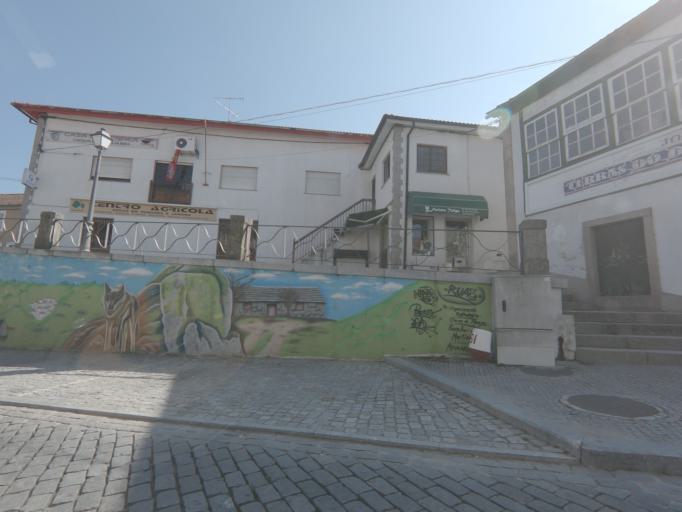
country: PT
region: Viseu
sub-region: Moimenta da Beira
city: Moimenta da Beira
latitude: 40.9809
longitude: -7.6151
